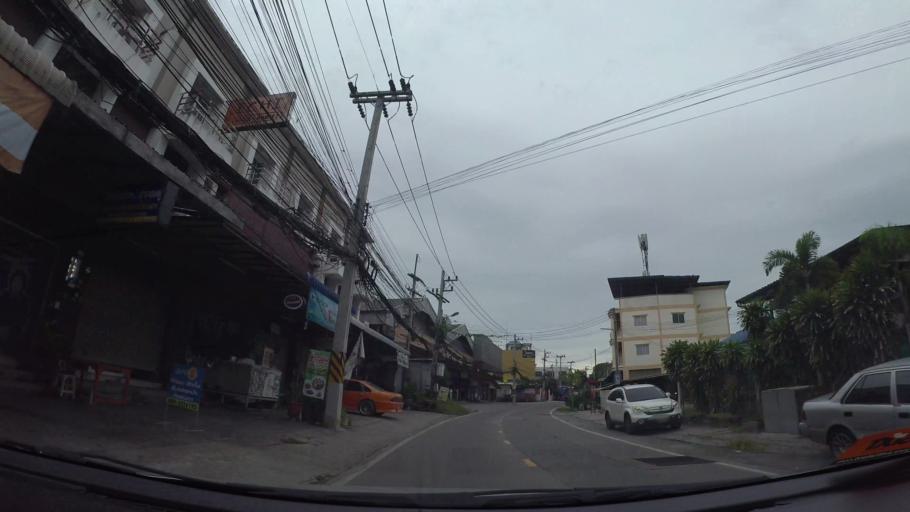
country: TH
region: Chon Buri
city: Si Racha
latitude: 13.1454
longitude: 100.9583
